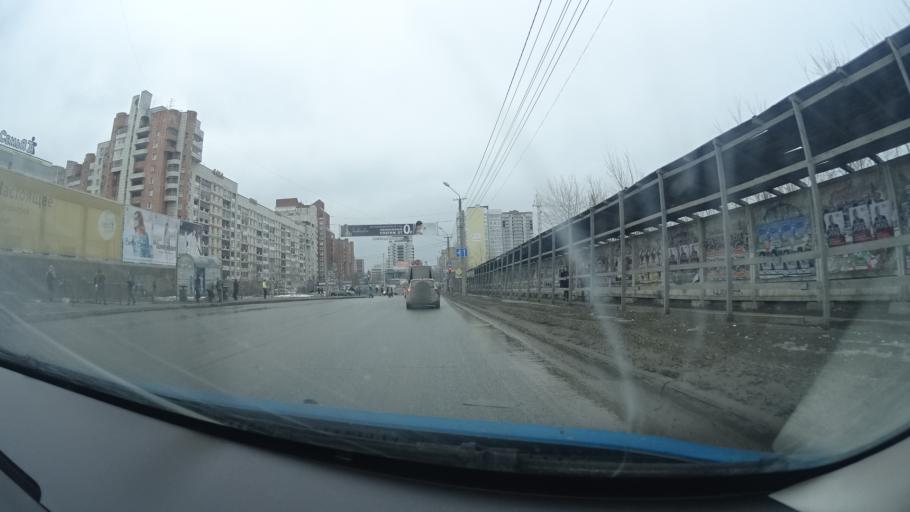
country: RU
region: Perm
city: Perm
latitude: 58.0077
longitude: 56.2640
